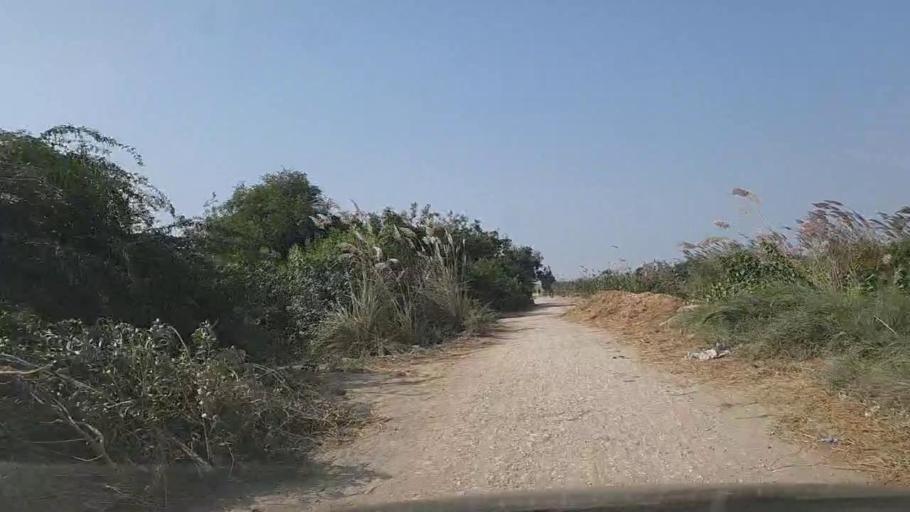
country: PK
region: Sindh
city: Gharo
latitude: 24.7030
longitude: 67.6403
